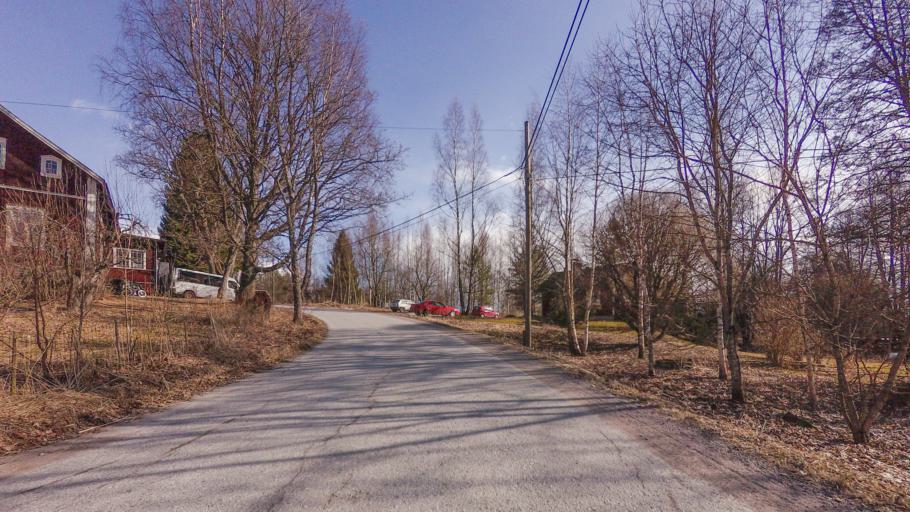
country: FI
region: Uusimaa
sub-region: Helsinki
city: Karjalohja
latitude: 60.2696
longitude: 23.6625
